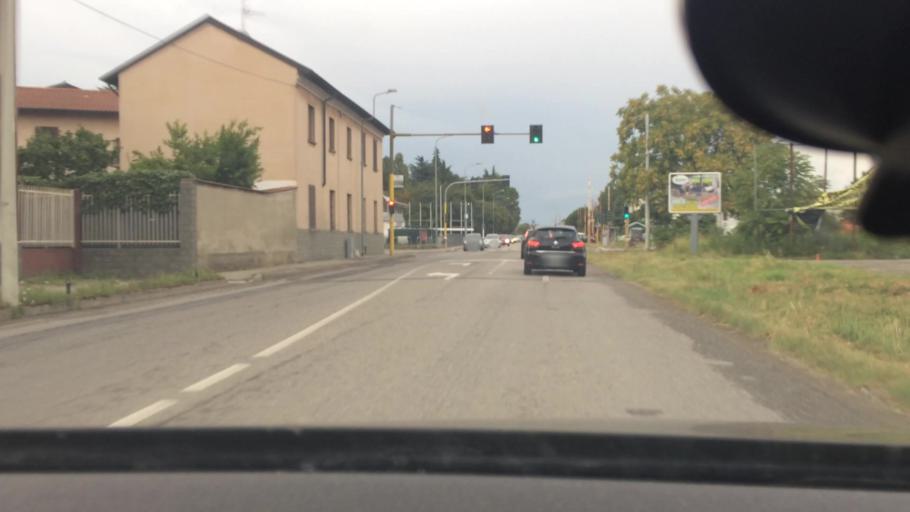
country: IT
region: Lombardy
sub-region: Citta metropolitana di Milano
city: Cusano Milanino
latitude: 45.5696
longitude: 9.1904
